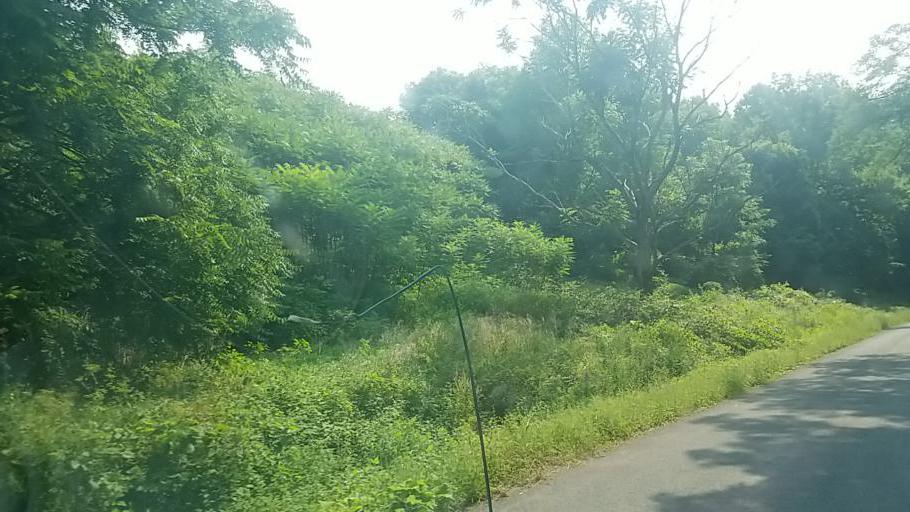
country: US
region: New York
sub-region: Montgomery County
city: Fonda
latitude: 42.9741
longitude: -74.4365
